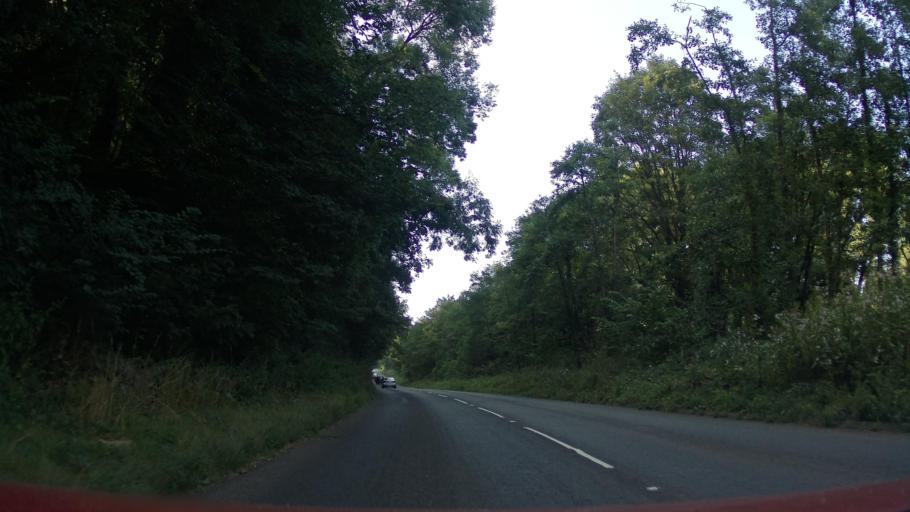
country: GB
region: England
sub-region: Devon
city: Tiverton
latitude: 50.8835
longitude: -3.4916
